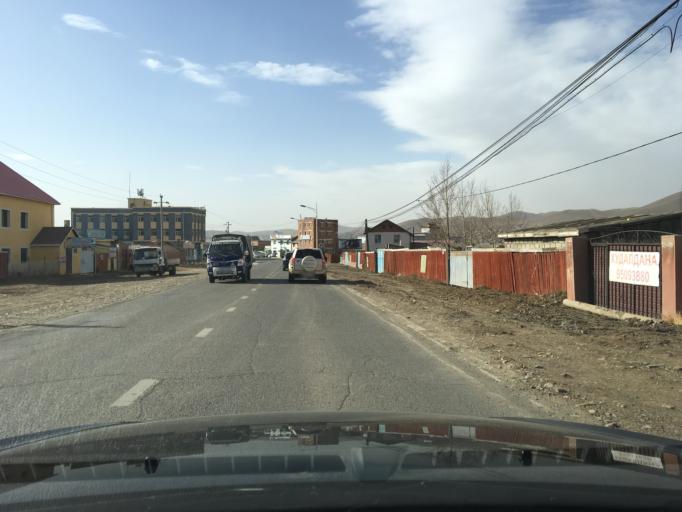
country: MN
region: Ulaanbaatar
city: Ulaanbaatar
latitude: 47.9832
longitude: 106.9413
